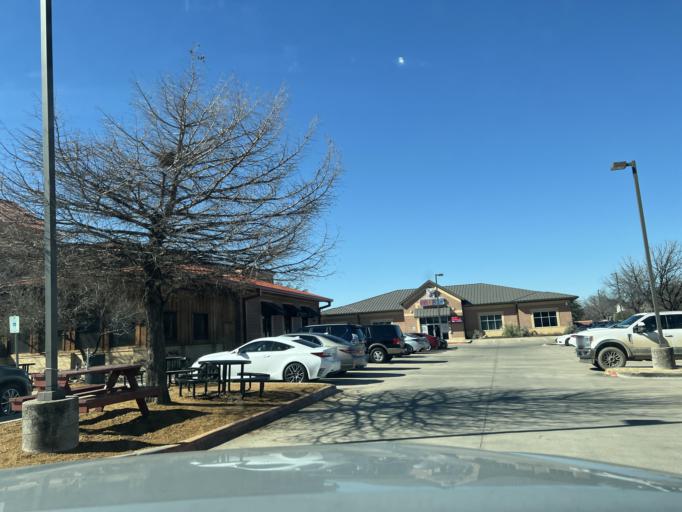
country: US
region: Texas
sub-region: Collin County
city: Frisco
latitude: 33.1548
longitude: -96.8045
